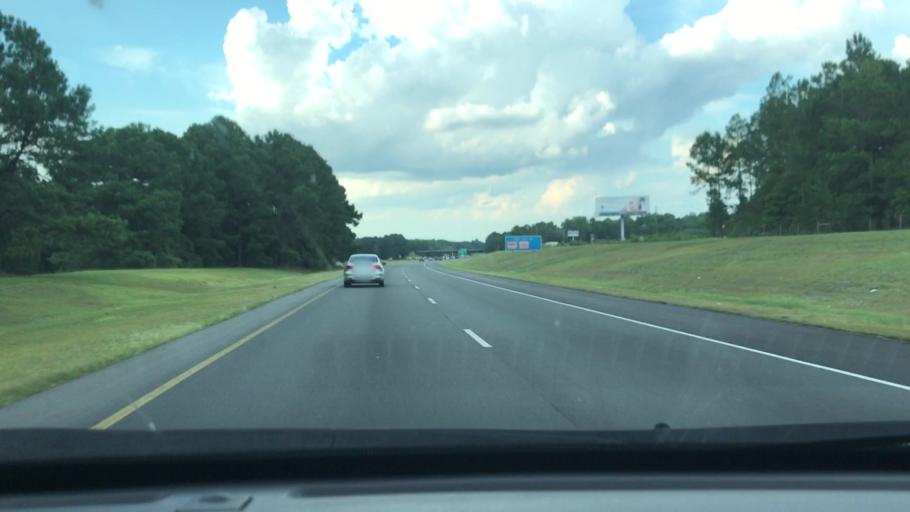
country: US
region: North Carolina
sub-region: Cumberland County
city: Eastover
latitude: 35.0755
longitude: -78.7902
